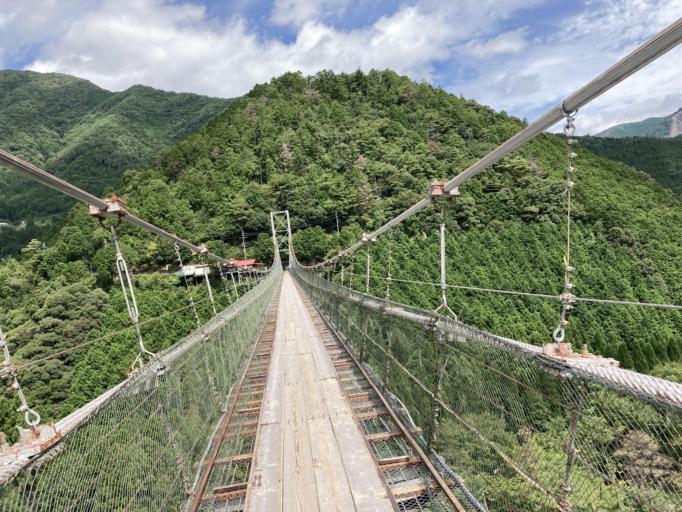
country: JP
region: Wakayama
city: Koya
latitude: 34.1016
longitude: 135.7629
